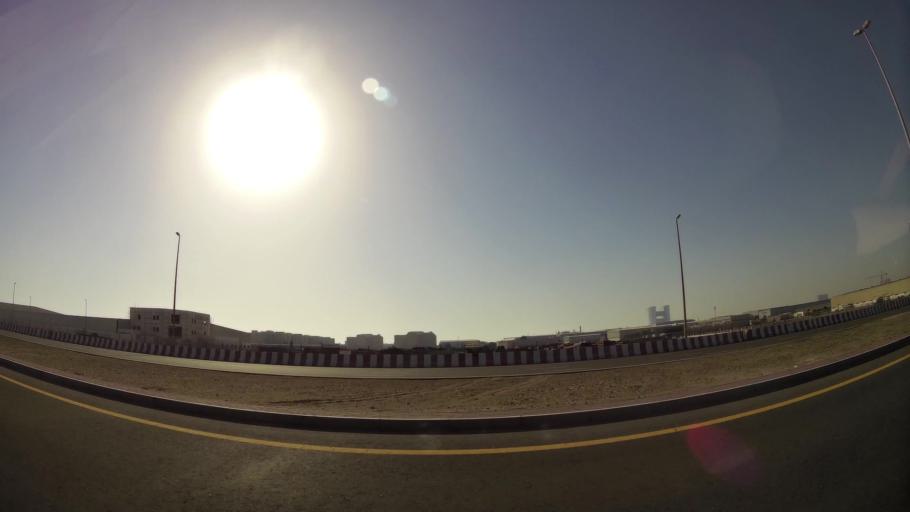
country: AE
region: Dubai
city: Dubai
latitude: 24.9470
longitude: 55.0900
